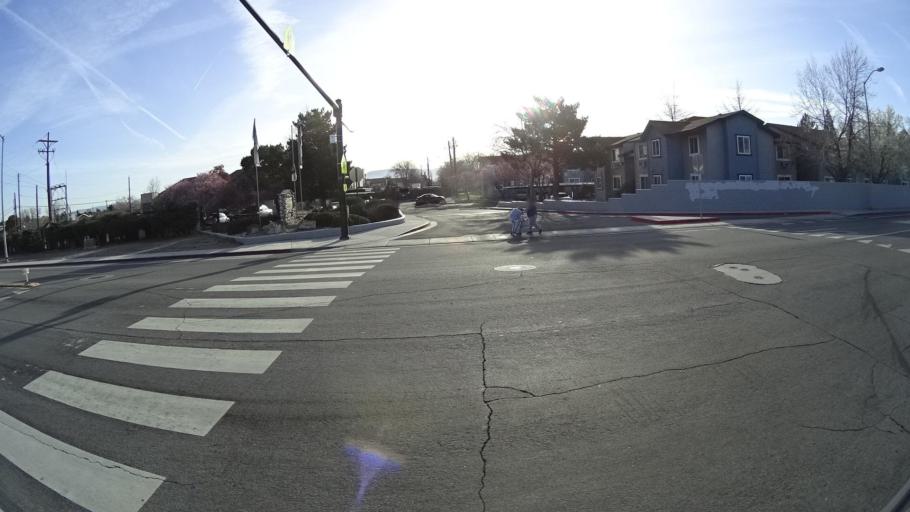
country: US
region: Nevada
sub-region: Washoe County
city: Sparks
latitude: 39.5409
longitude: -119.7761
